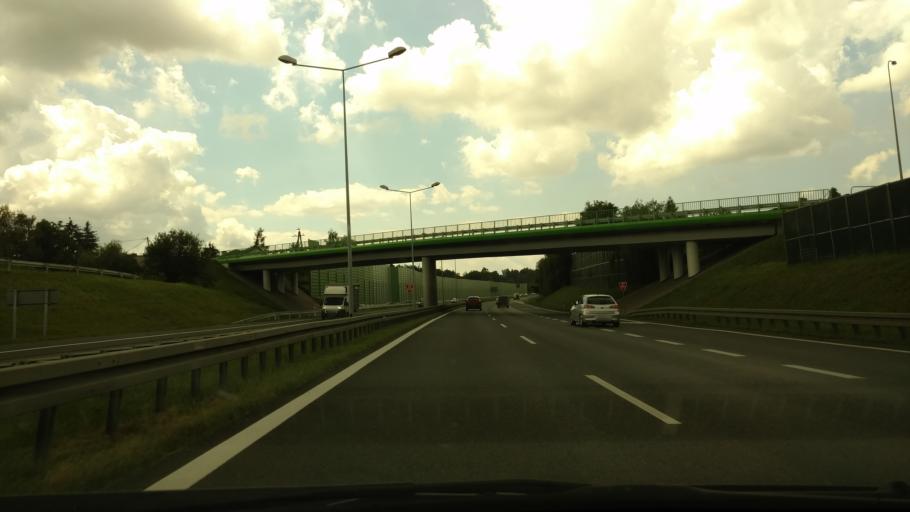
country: PL
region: Lesser Poland Voivodeship
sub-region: Powiat krakowski
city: Rzaska
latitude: 50.1037
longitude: 19.8368
